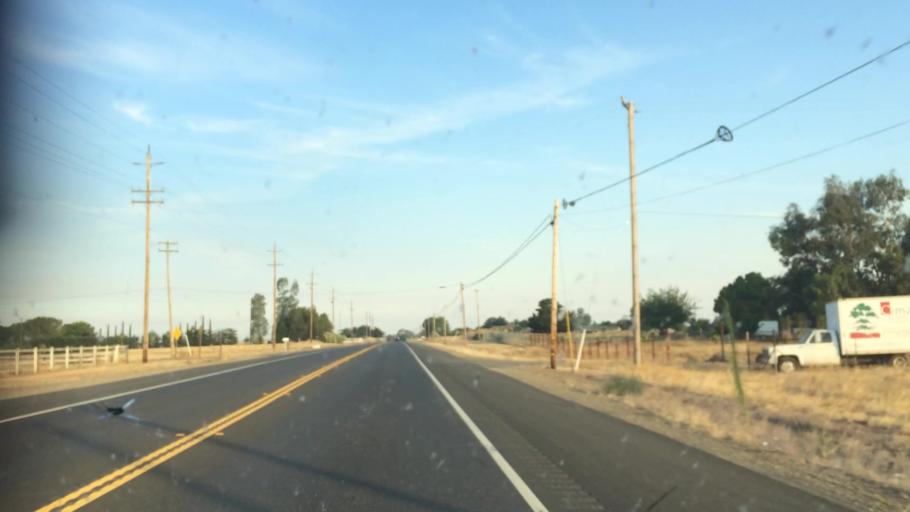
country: US
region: California
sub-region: Sacramento County
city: Wilton
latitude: 38.4990
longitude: -121.2094
